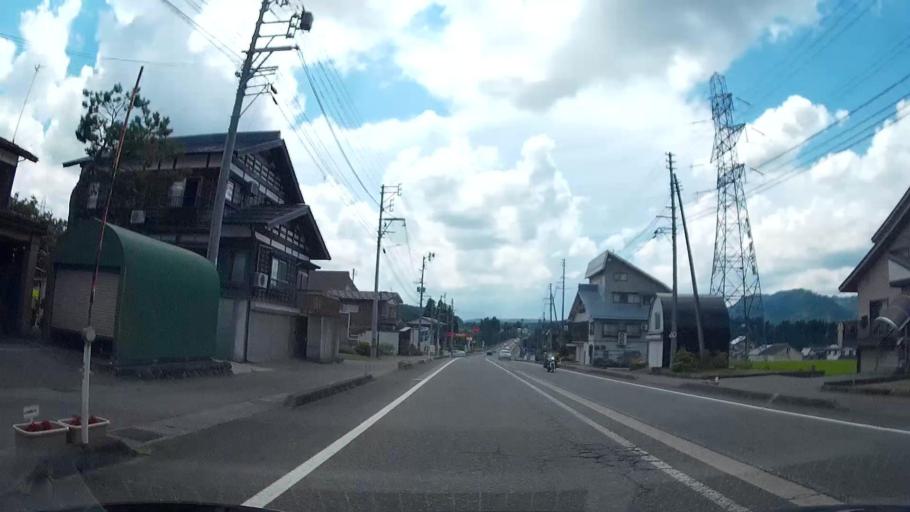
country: JP
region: Niigata
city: Tokamachi
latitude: 37.0477
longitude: 138.6916
